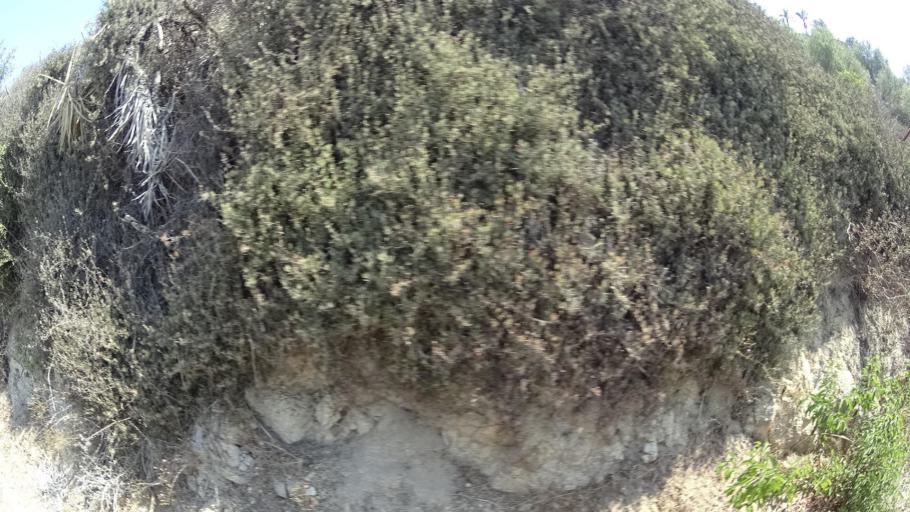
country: US
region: California
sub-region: San Diego County
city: Fallbrook
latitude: 33.4376
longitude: -117.2865
